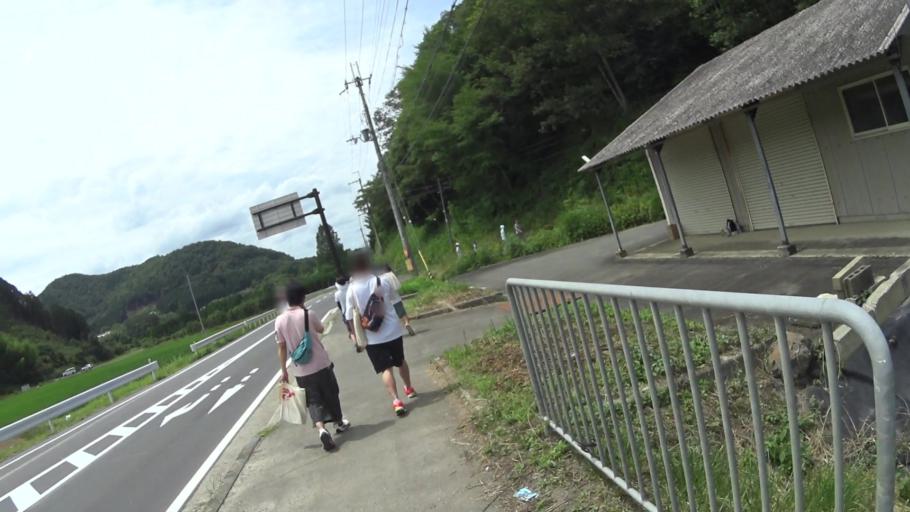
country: JP
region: Kyoto
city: Ayabe
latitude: 35.1588
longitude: 135.4148
